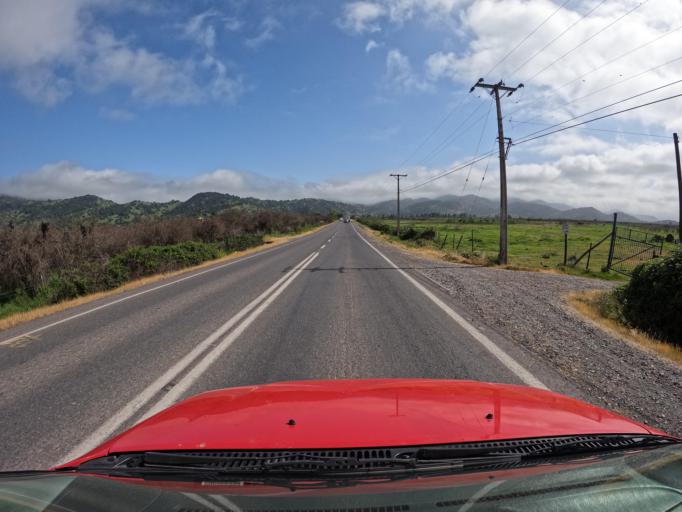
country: CL
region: Maule
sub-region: Provincia de Curico
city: Teno
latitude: -34.8400
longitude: -71.1871
